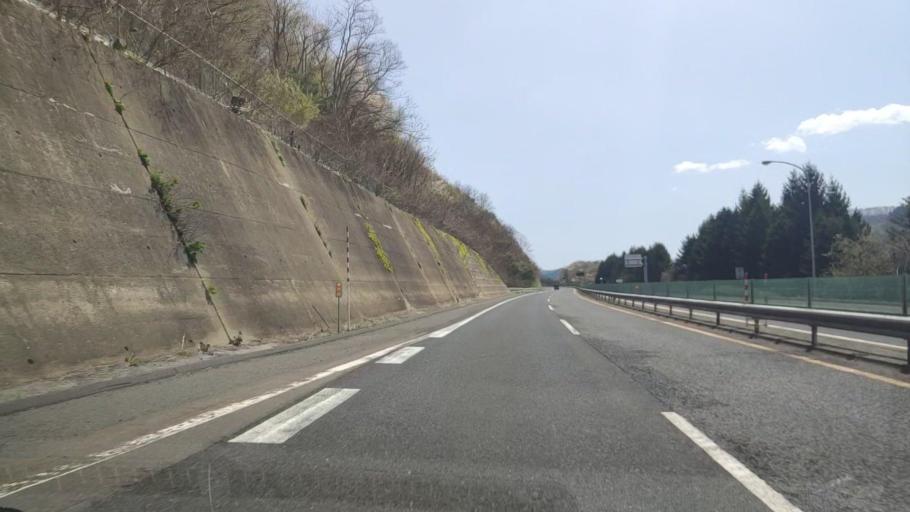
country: JP
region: Iwate
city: Ichinohe
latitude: 40.2325
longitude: 141.3013
